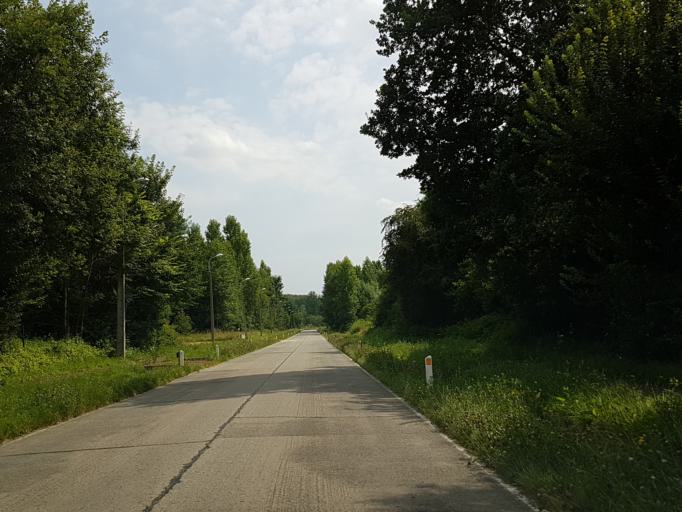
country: BE
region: Flanders
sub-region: Provincie Vlaams-Brabant
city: Herent
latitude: 50.9185
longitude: 4.6369
